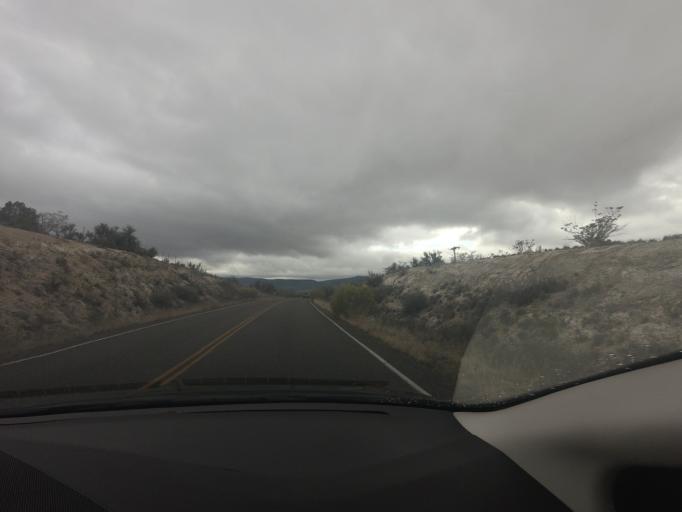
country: US
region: Arizona
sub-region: Yavapai County
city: Camp Verde
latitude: 34.6159
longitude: -111.8439
